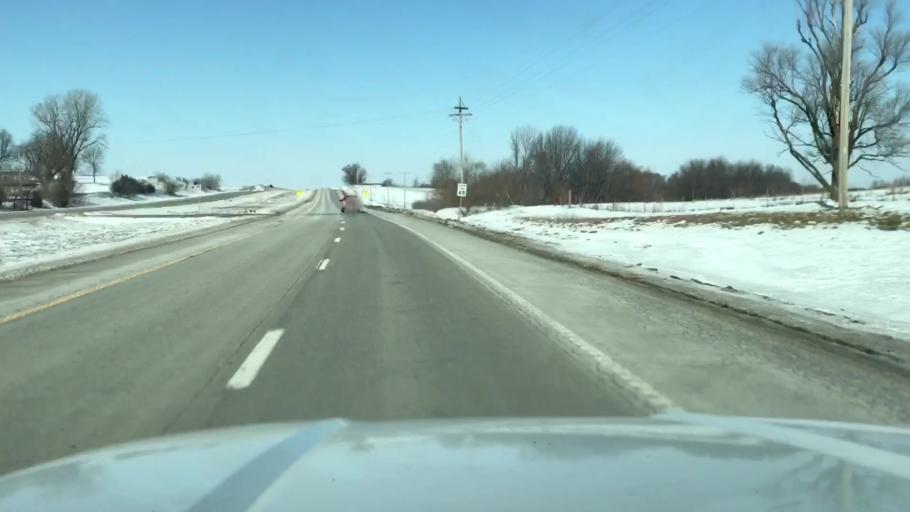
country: US
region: Missouri
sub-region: Andrew County
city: Savannah
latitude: 39.9659
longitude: -94.8657
